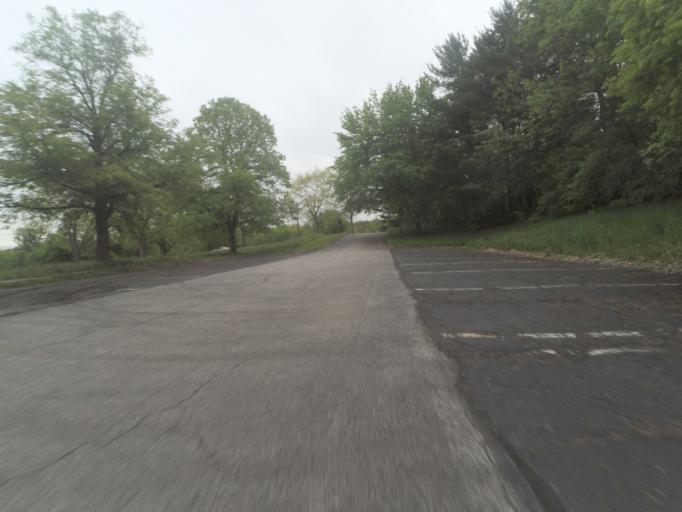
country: US
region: Ohio
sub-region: Portage County
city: Kent
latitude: 41.1404
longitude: -81.3453
